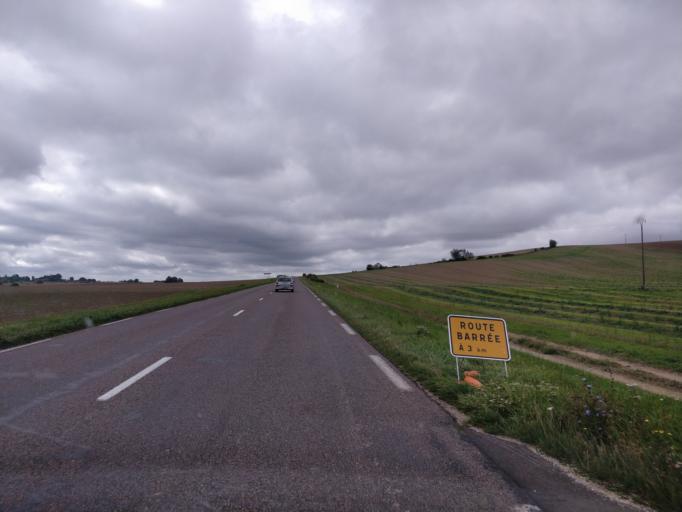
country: FR
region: Champagne-Ardenne
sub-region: Departement de l'Aube
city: Bouilly
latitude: 48.1398
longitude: 4.0027
